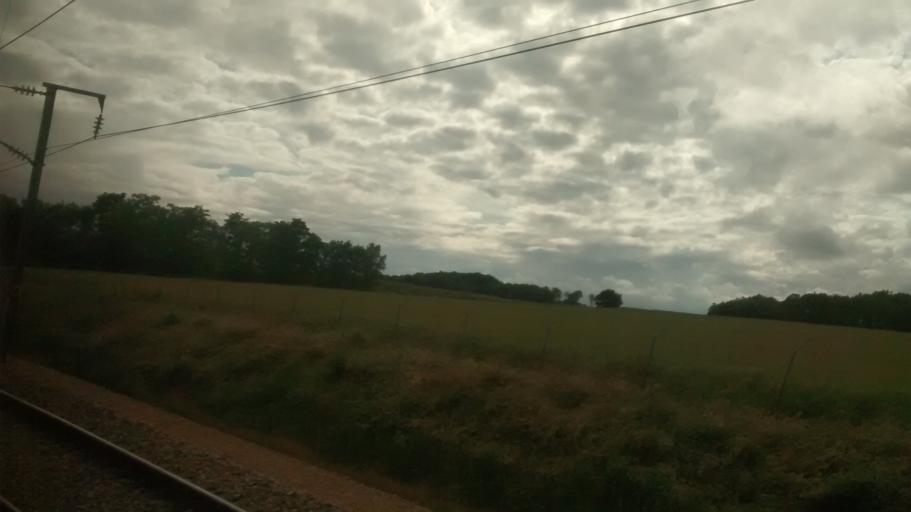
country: FR
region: Centre
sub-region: Departement d'Eure-et-Loir
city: Arrou
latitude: 48.1216
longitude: 1.1803
